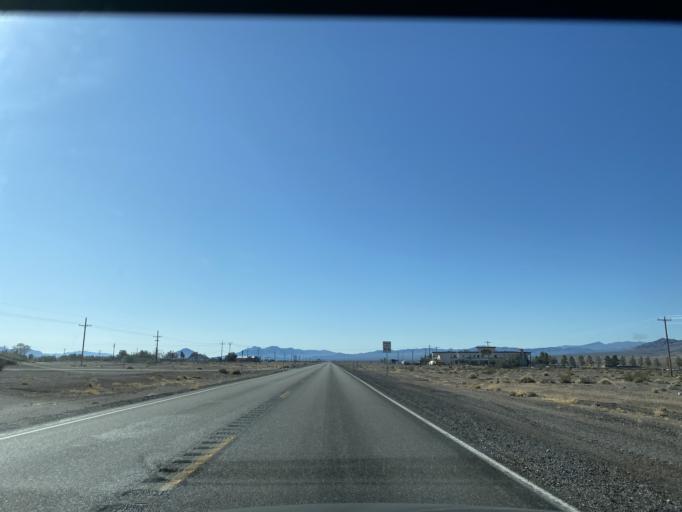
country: US
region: Nevada
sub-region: Nye County
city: Pahrump
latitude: 36.4168
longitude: -116.4222
